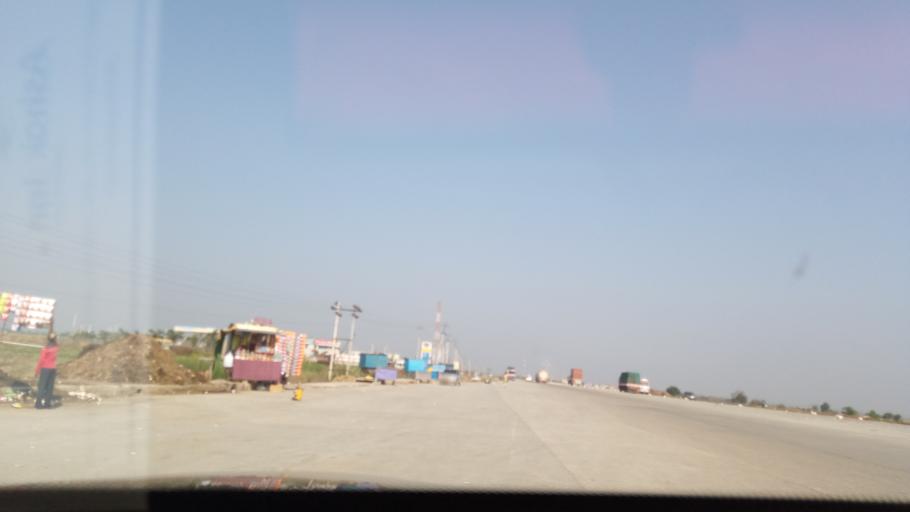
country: IN
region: Karnataka
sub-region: Haveri
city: Savanur
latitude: 14.9109
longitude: 75.2786
